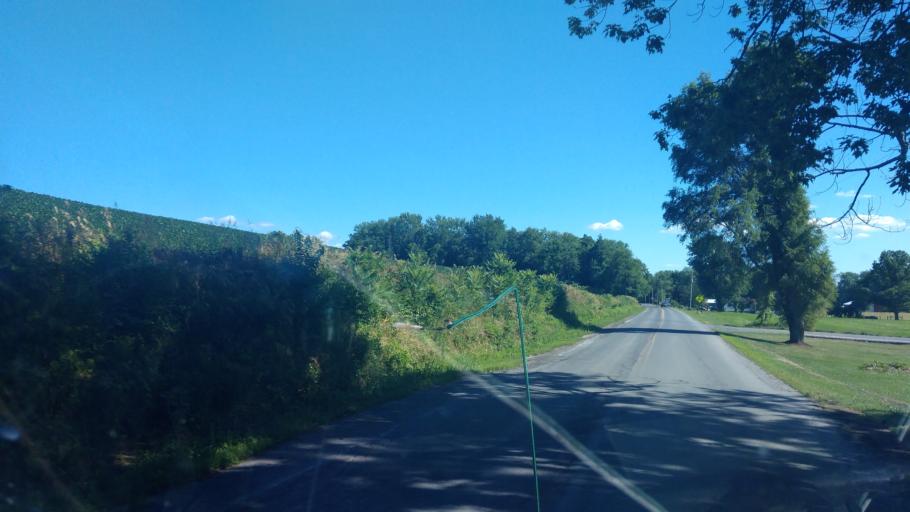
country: US
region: New York
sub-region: Wayne County
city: Clyde
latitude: 43.0143
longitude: -76.8116
